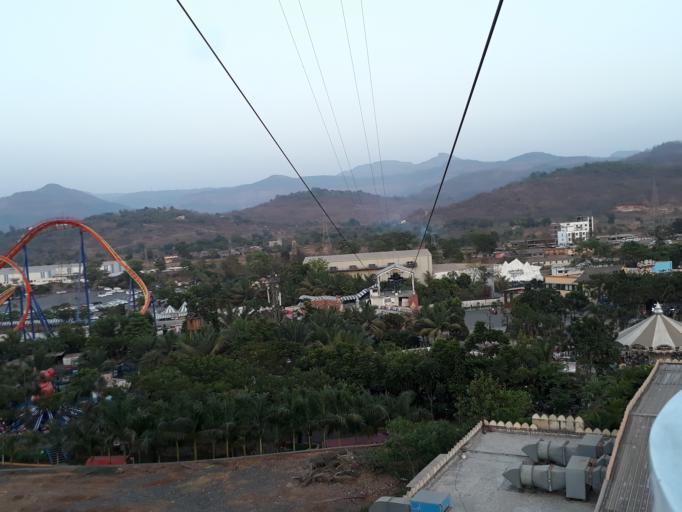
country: IN
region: Maharashtra
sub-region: Raigarh
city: Khopoli
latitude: 18.7679
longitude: 73.2798
